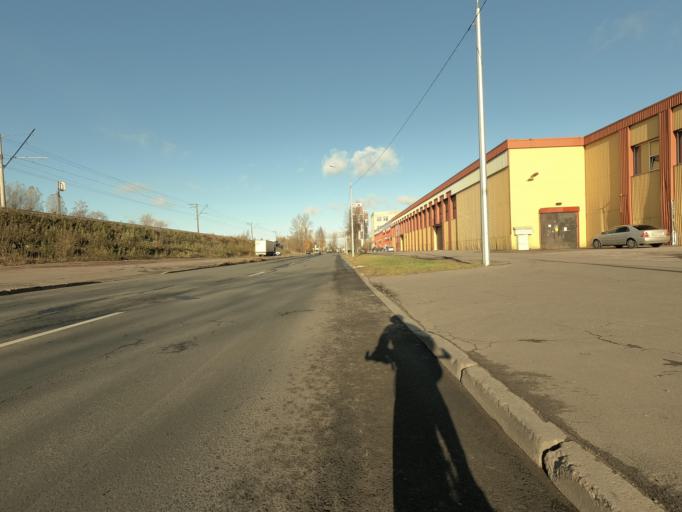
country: RU
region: St.-Petersburg
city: Krasnogvargeisky
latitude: 59.9513
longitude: 30.4477
